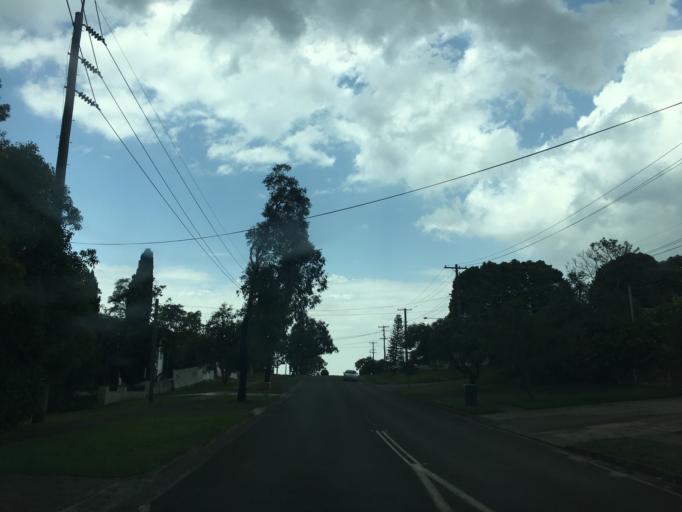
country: AU
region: New South Wales
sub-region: Ryde
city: Marsfield
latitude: -33.7913
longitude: 151.1063
